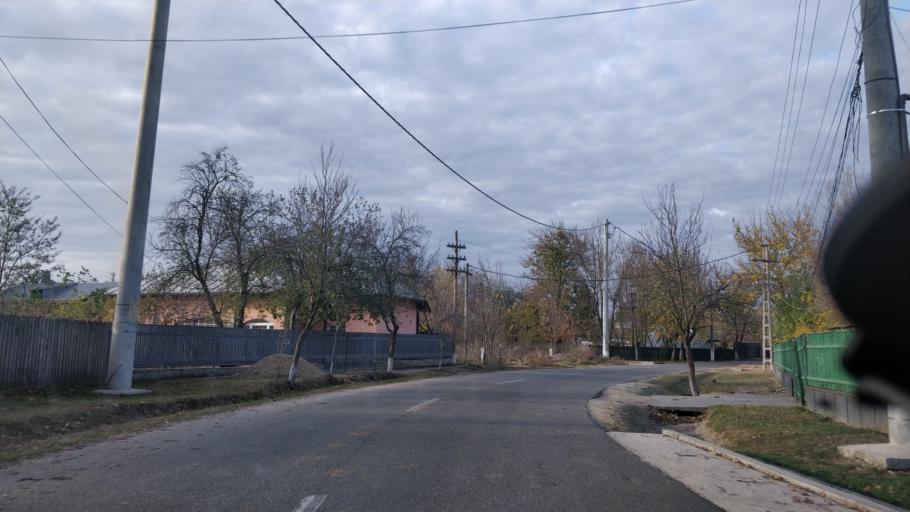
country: RO
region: Giurgiu
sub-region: Comuna Bucsani
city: Bucsani
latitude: 44.3477
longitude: 25.6549
